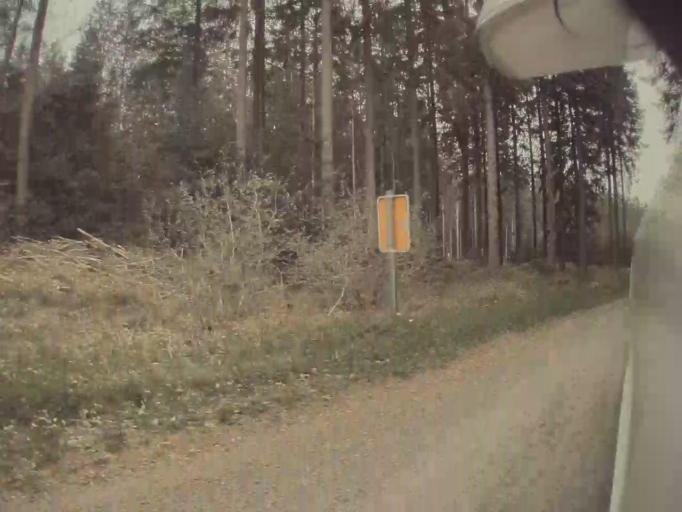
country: BE
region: Wallonia
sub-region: Province du Luxembourg
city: La Roche-en-Ardenne
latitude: 50.2373
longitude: 5.5950
